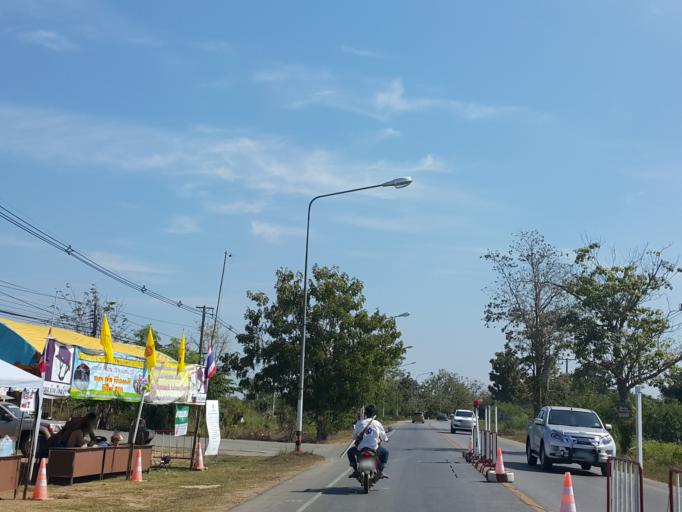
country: TH
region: Sukhothai
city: Thung Saliam
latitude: 17.3178
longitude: 99.6846
